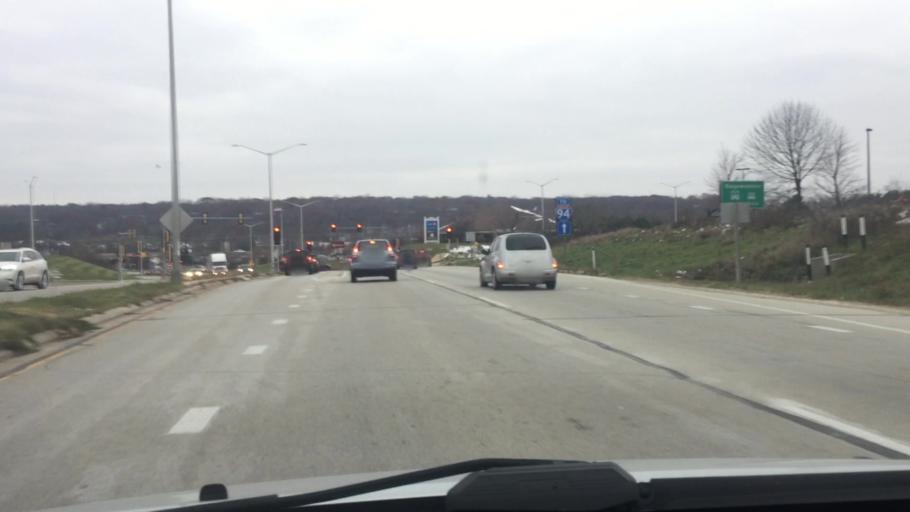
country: US
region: Wisconsin
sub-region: Waukesha County
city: Delafield
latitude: 43.0551
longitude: -88.3707
